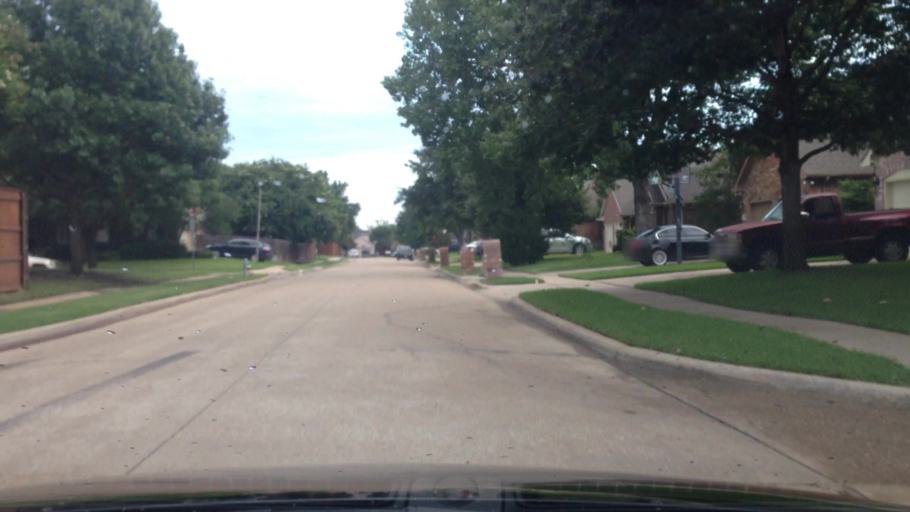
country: US
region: Texas
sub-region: Denton County
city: Flower Mound
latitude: 33.0165
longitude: -97.0560
